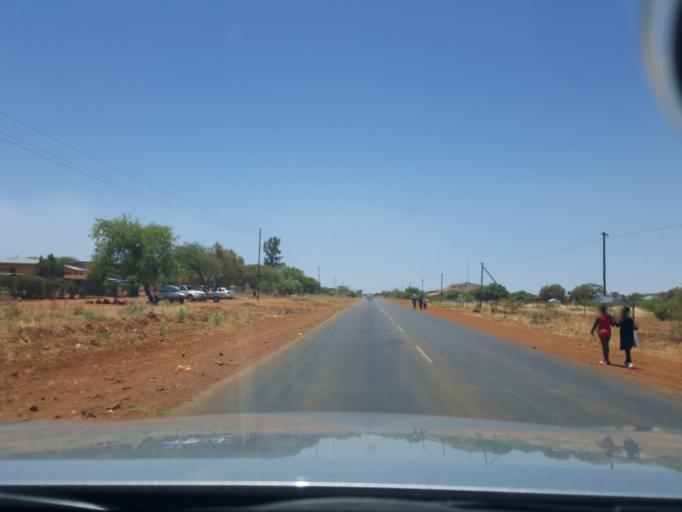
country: ZA
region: North-West
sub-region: Ngaka Modiri Molema District Municipality
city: Zeerust
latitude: -25.4633
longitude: 25.9720
